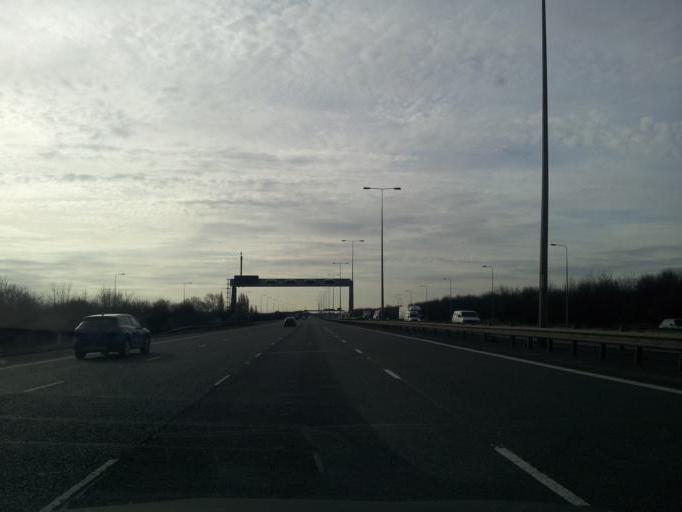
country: GB
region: England
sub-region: Cambridgeshire
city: Sawtry
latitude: 52.4335
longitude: -0.2716
